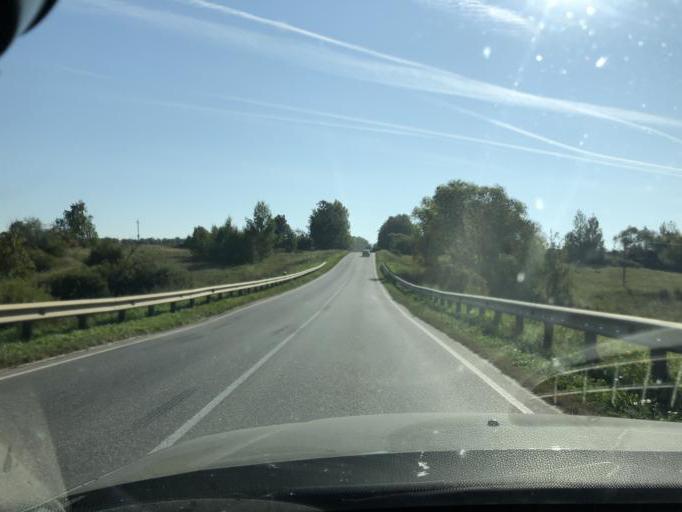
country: RU
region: Tula
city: Yasnogorsk
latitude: 54.4702
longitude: 37.5887
